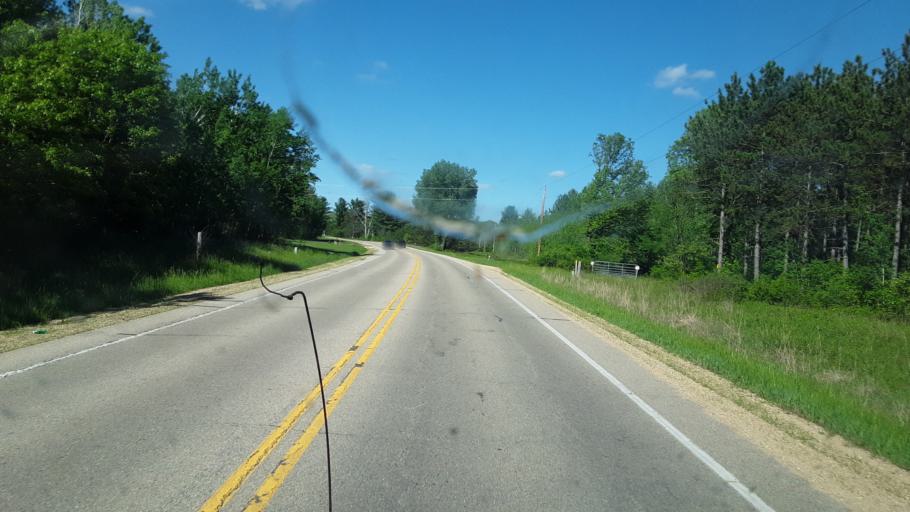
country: US
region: Wisconsin
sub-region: Juneau County
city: New Lisbon
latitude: 43.8938
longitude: -90.1383
